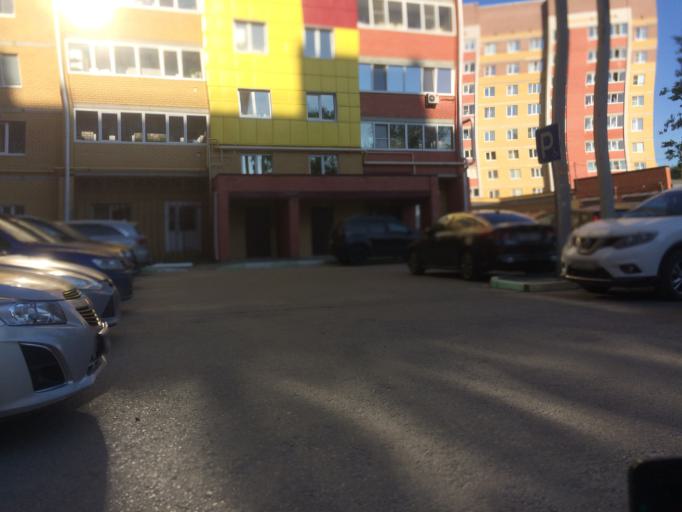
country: RU
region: Mariy-El
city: Yoshkar-Ola
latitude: 56.6459
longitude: 47.8550
